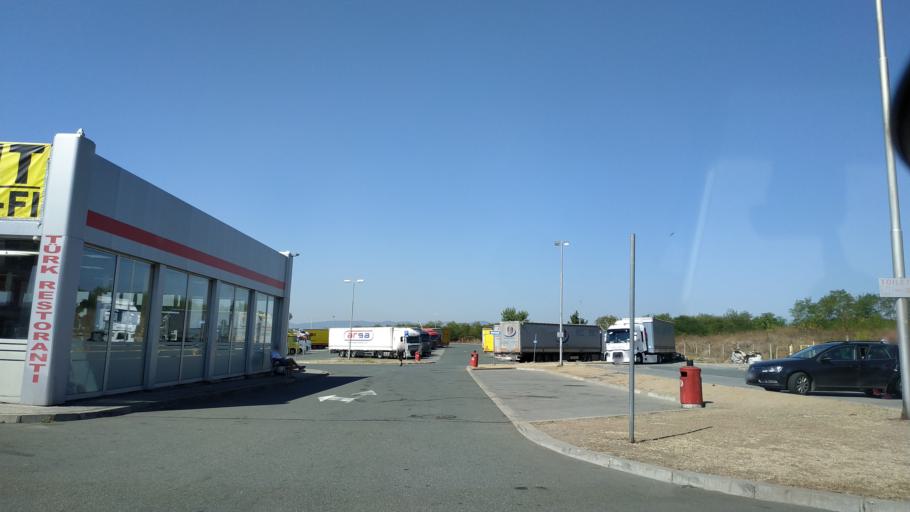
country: RS
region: Central Serbia
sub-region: Rasinski Okrug
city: Cicevac
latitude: 43.7510
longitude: 21.4492
